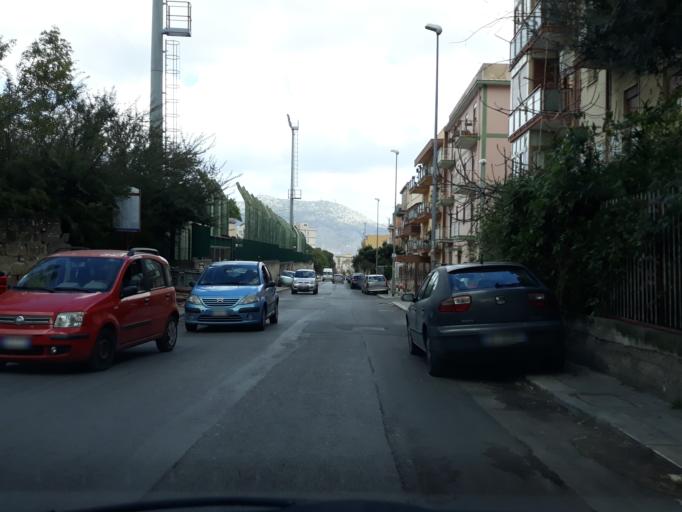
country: IT
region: Sicily
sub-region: Palermo
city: Palermo
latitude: 38.1206
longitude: 13.3064
